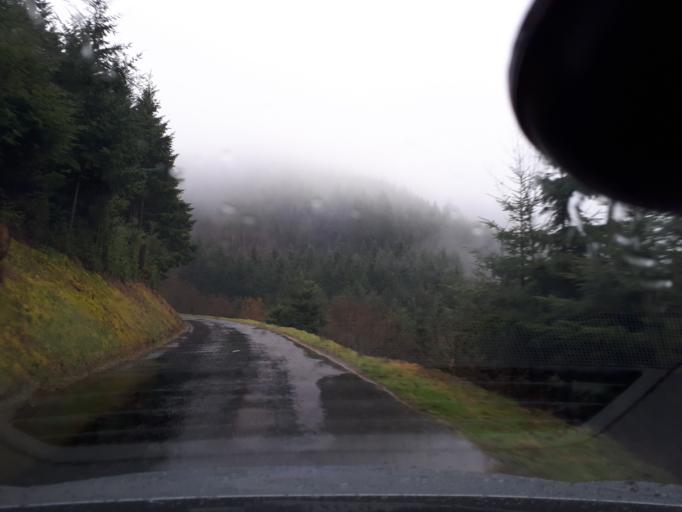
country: FR
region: Rhone-Alpes
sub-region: Departement du Rhone
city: Tarare
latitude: 45.9464
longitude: 4.4014
